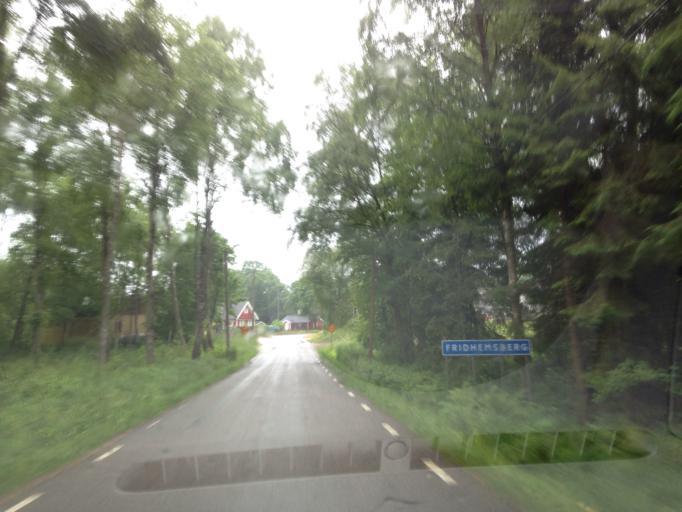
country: SE
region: Vaestra Goetaland
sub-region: Marks Kommun
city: Horred
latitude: 57.1648
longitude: 12.7444
